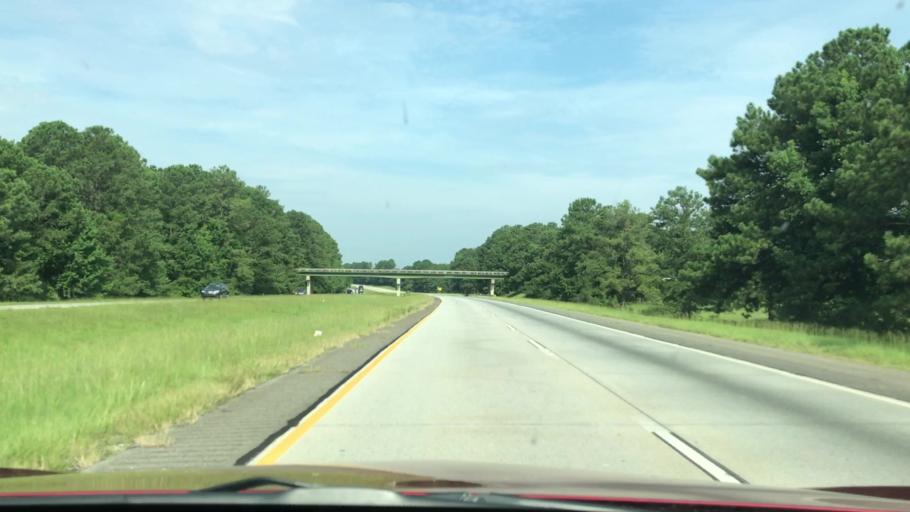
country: US
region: Georgia
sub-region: Warren County
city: Firing Range
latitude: 33.5020
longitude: -82.7105
